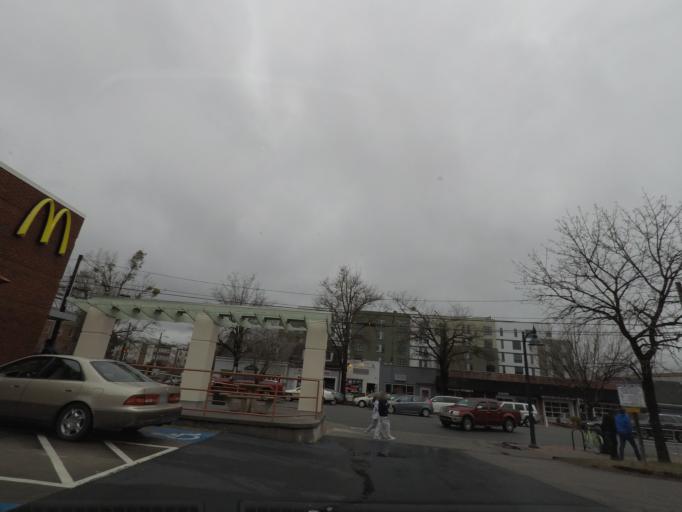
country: US
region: North Carolina
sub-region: Orange County
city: Chapel Hill
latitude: 35.9109
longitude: -79.0610
